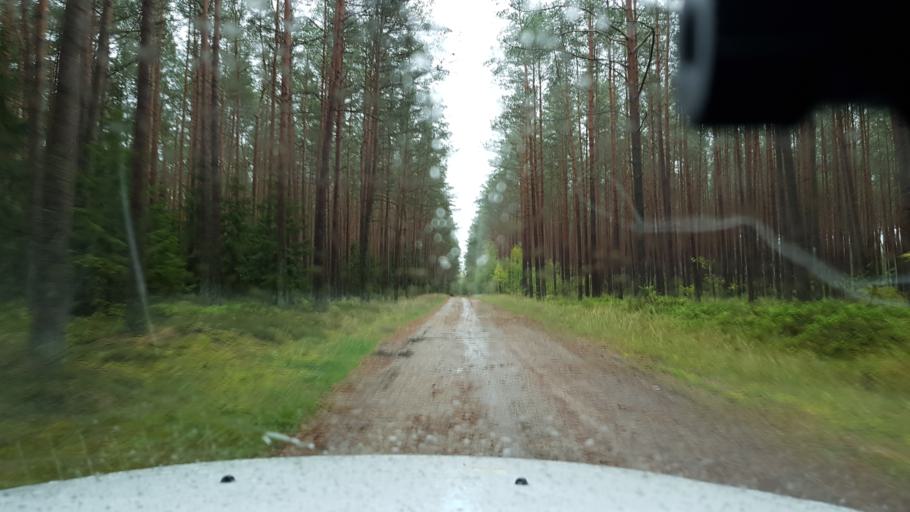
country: PL
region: West Pomeranian Voivodeship
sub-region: Powiat goleniowski
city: Przybiernow
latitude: 53.7296
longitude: 14.8080
